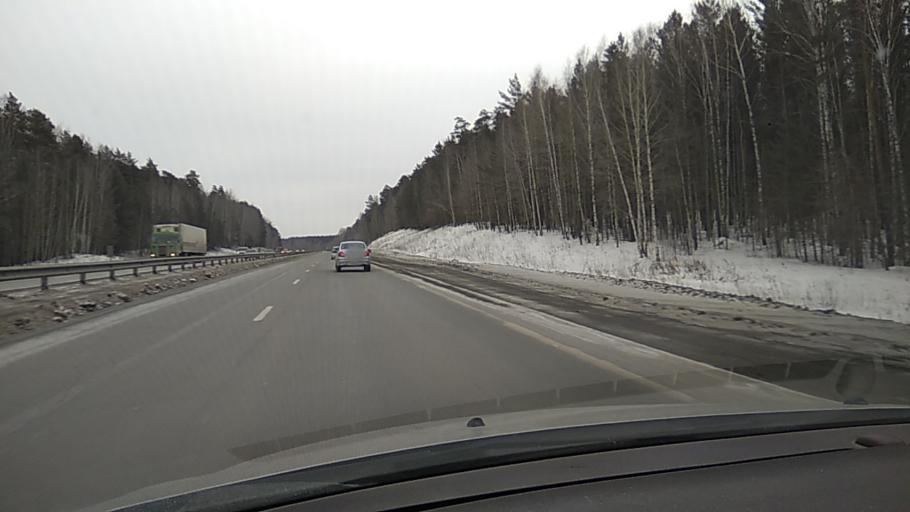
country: RU
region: Sverdlovsk
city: Talitsa
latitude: 56.8431
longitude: 60.0948
